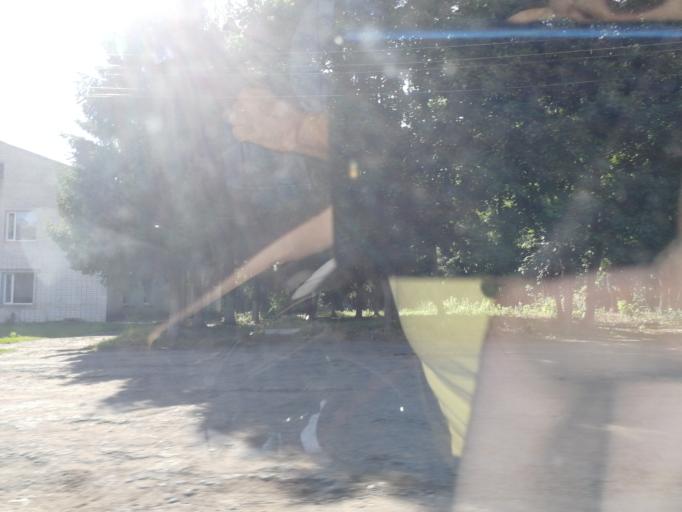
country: RU
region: Tula
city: Tovarkovskiy
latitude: 53.6141
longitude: 38.2702
